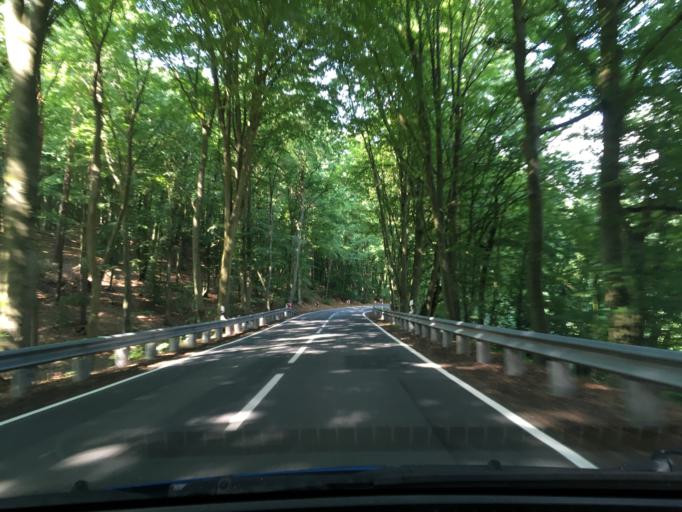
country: DE
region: Lower Saxony
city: Tosterglope
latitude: 53.2353
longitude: 10.8376
